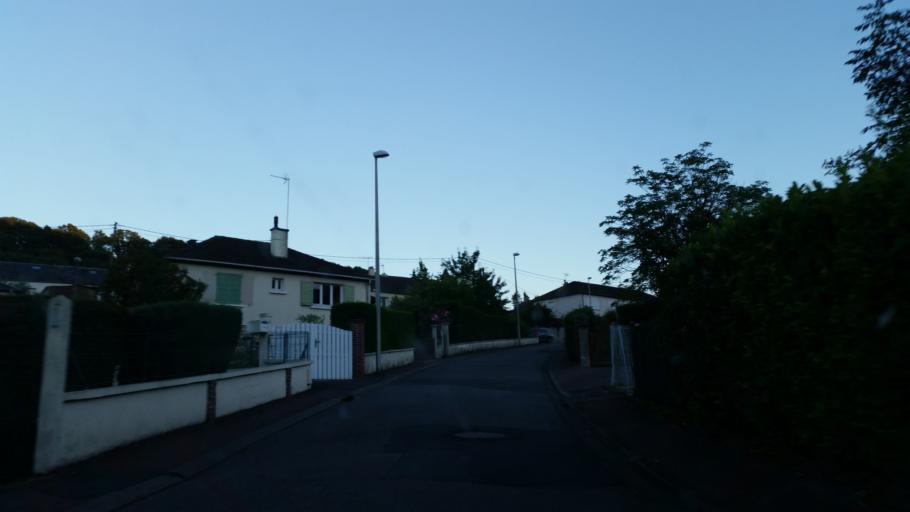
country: FR
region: Lower Normandy
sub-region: Departement du Calvados
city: Honfleur
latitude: 49.4124
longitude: 0.2281
